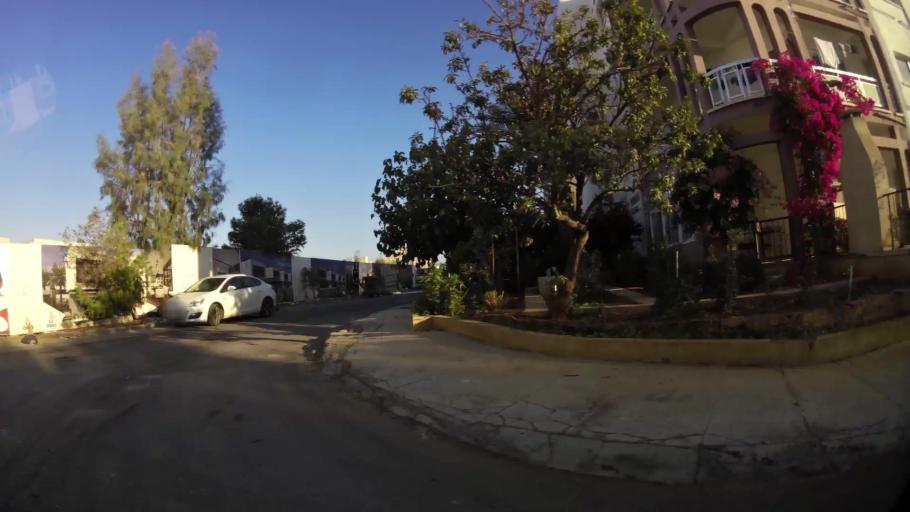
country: CY
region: Lefkosia
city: Nicosia
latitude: 35.2052
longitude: 33.3070
